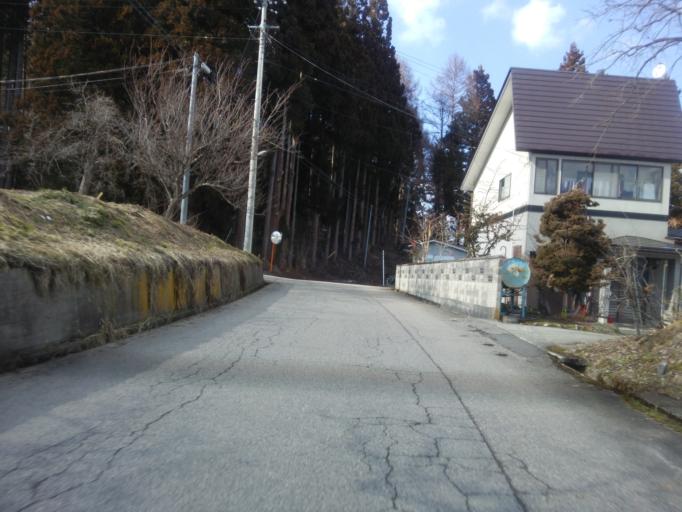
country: JP
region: Fukushima
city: Kitakata
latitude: 37.4508
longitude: 139.7993
